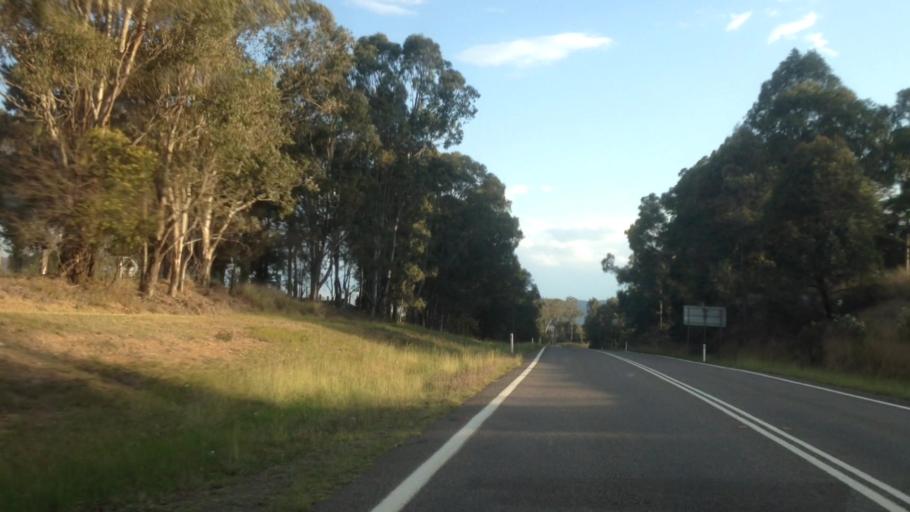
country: AU
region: New South Wales
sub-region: Cessnock
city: Kurri Kurri
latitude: -32.8662
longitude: 151.4800
